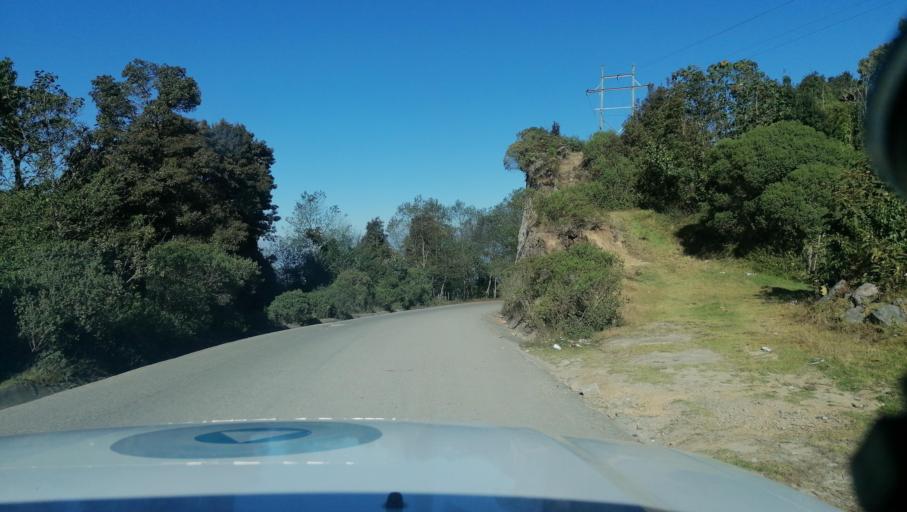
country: MX
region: Chiapas
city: Motozintla de Mendoza
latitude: 15.2630
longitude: -92.2179
